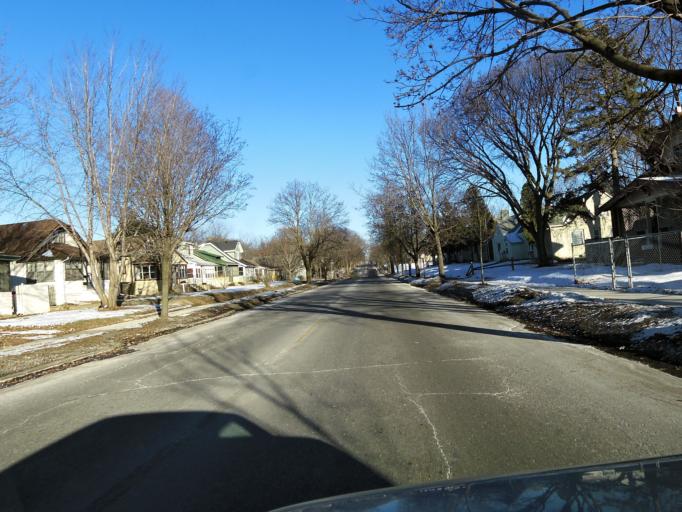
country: US
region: Minnesota
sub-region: Ramsey County
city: Maplewood
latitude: 44.9630
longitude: -93.0326
